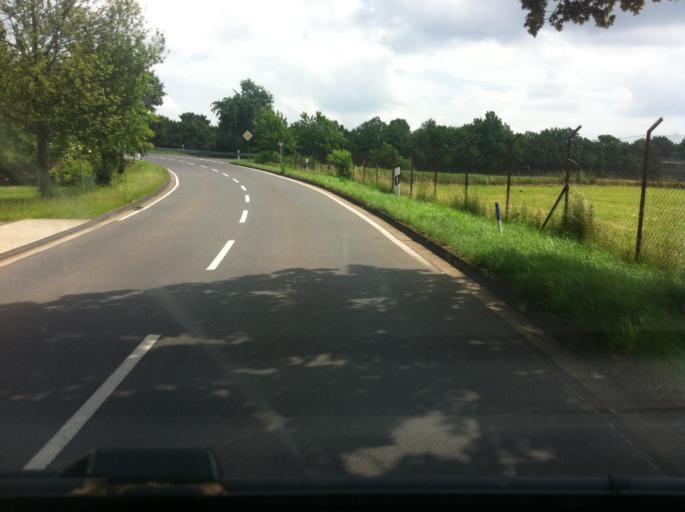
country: DE
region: North Rhine-Westphalia
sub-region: Regierungsbezirk Koln
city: Euskirchen
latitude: 50.6588
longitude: 6.8431
